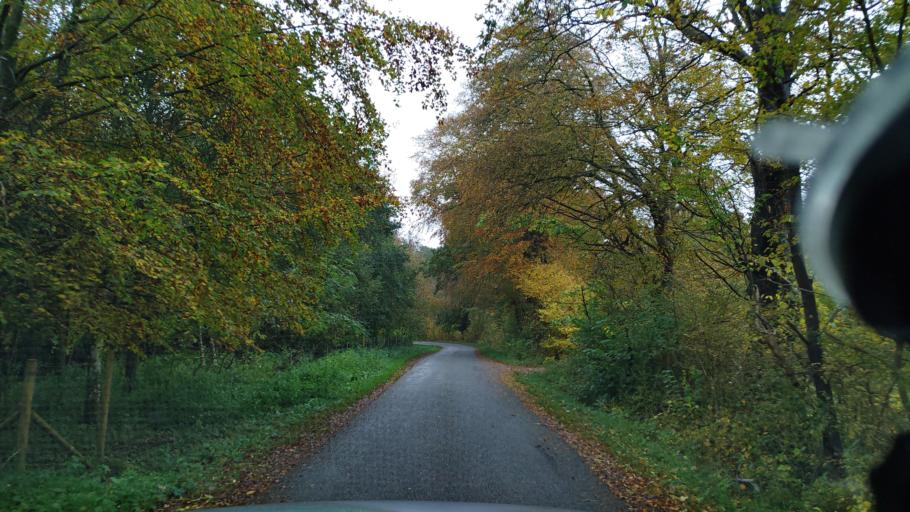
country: DK
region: Zealand
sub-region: Faxe Kommune
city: Ronnede
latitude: 55.2419
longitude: 11.9450
